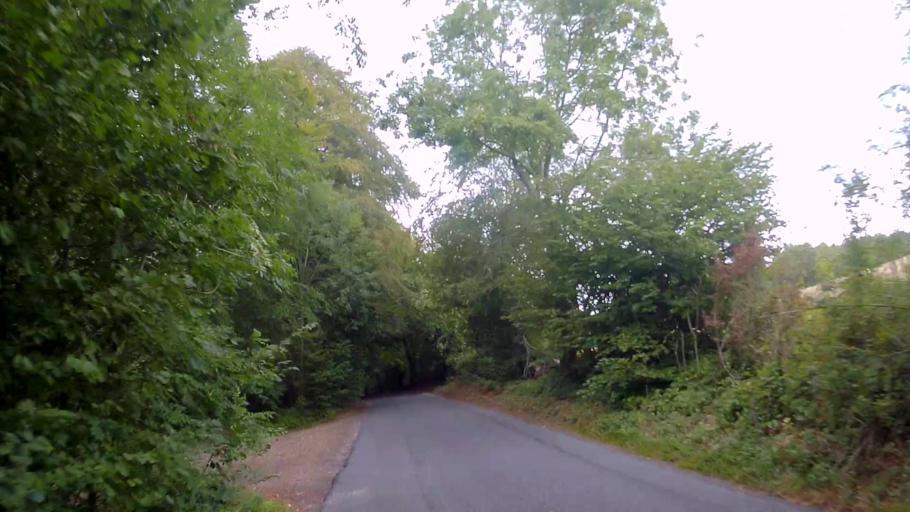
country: GB
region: England
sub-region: Hampshire
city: Overton
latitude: 51.1922
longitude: -1.2791
